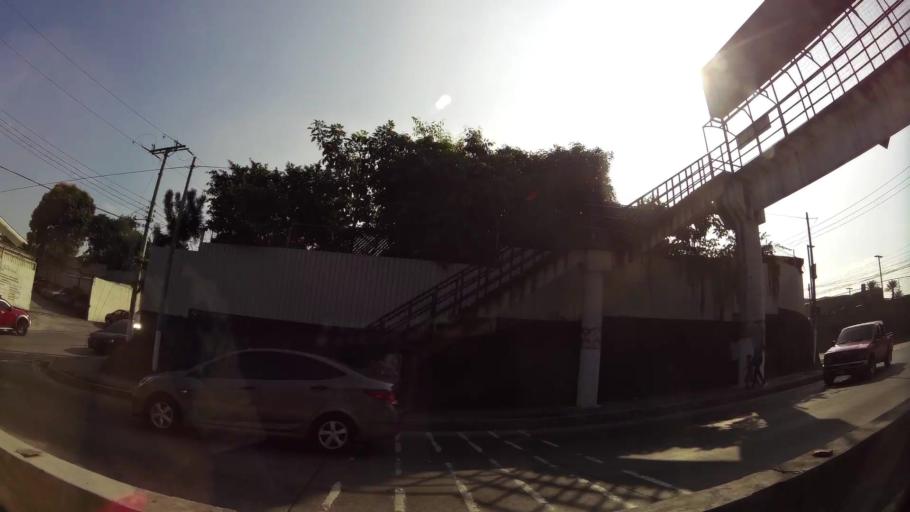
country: SV
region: La Libertad
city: Antiguo Cuscatlan
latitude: 13.6674
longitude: -89.2234
